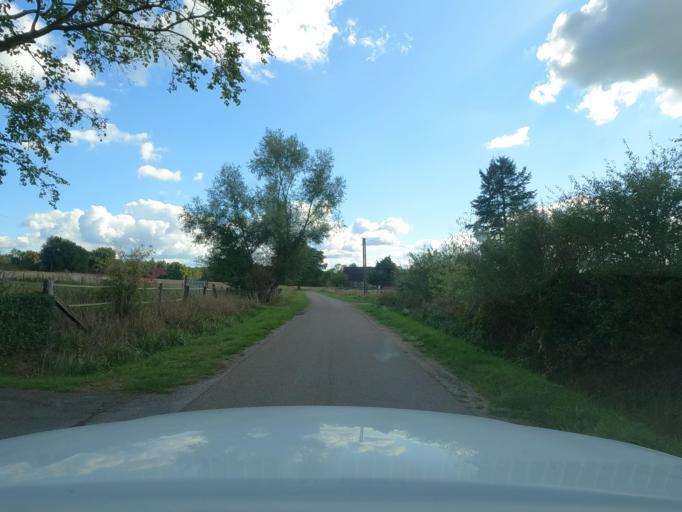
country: DE
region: North Rhine-Westphalia
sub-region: Regierungsbezirk Dusseldorf
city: Hunxe
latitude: 51.6550
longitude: 6.8011
